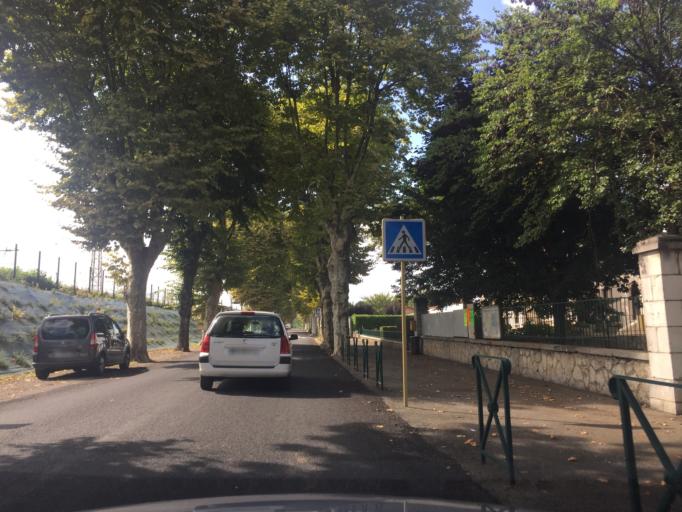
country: FR
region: Midi-Pyrenees
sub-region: Departement de la Haute-Garonne
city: Gourdan-Polignan
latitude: 43.0775
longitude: 0.5781
